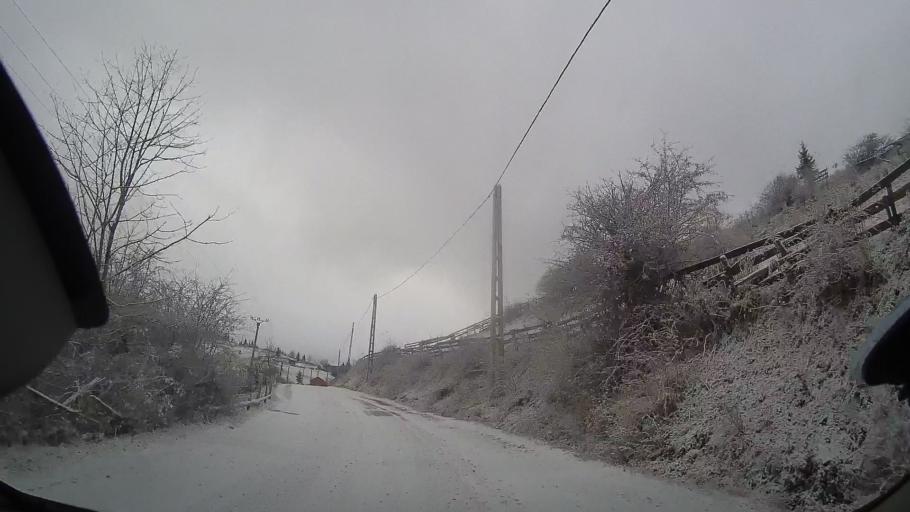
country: RO
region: Cluj
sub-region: Comuna Marisel
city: Marisel
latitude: 46.6603
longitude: 23.1495
